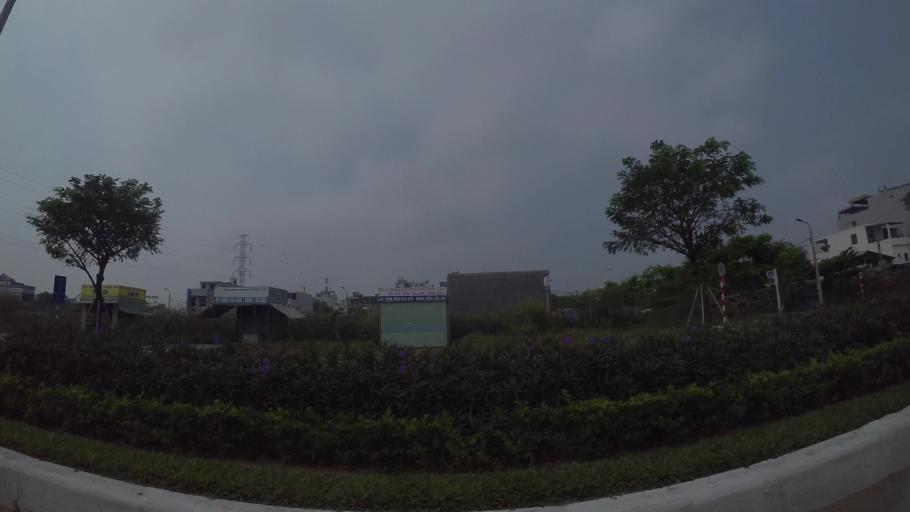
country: VN
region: Da Nang
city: Cam Le
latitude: 16.0087
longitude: 108.2189
